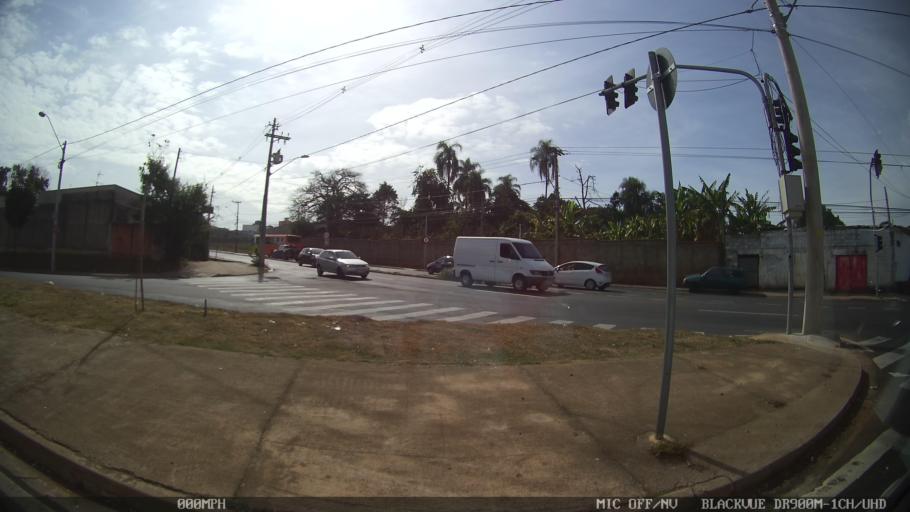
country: BR
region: Sao Paulo
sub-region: Piracicaba
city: Piracicaba
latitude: -22.7486
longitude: -47.6220
